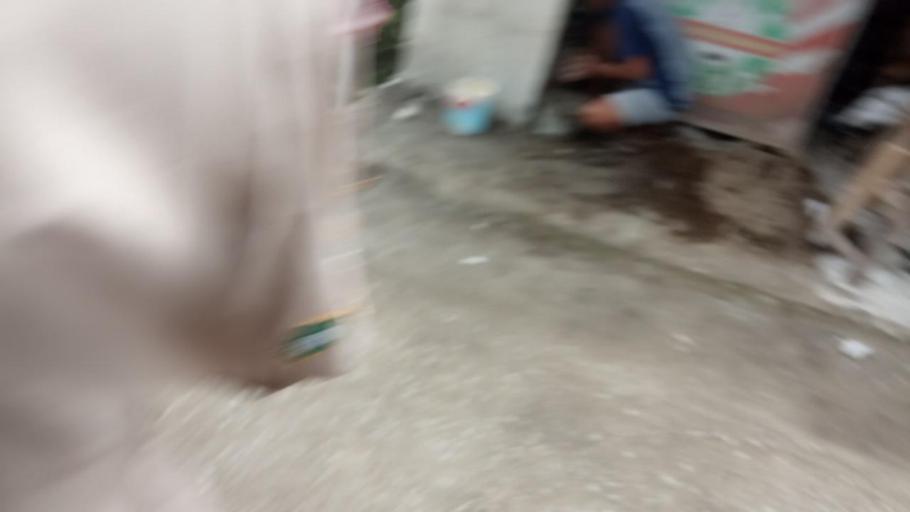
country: ID
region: West Java
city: Caringin
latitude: -6.6526
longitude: 106.8962
